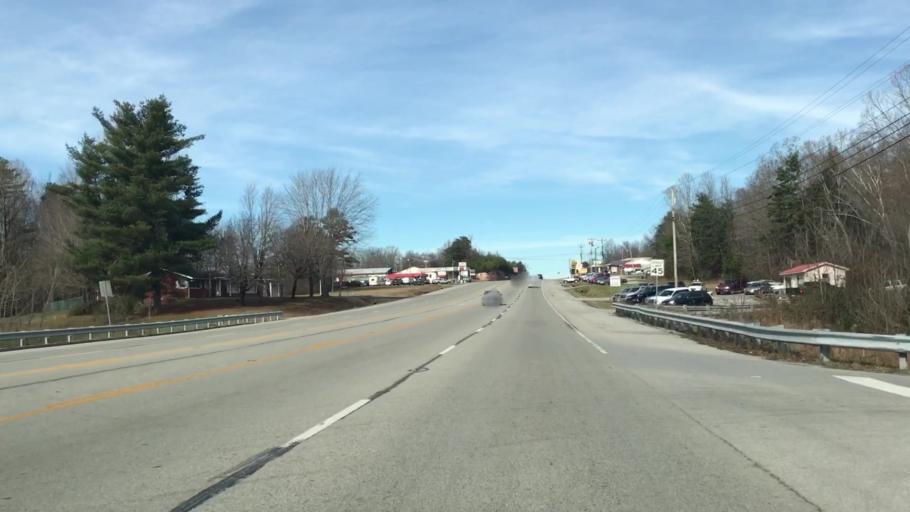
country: US
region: Kentucky
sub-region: McCreary County
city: Whitley City
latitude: 36.7309
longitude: -84.4696
